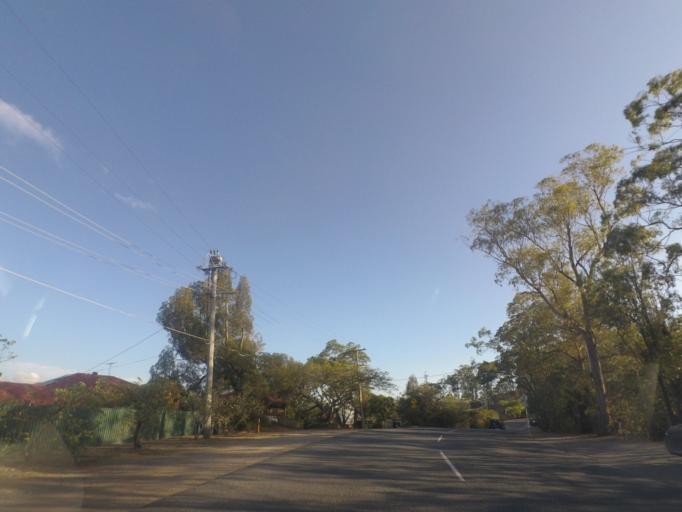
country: AU
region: Queensland
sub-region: Brisbane
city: Taringa
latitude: -27.4718
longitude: 152.9719
